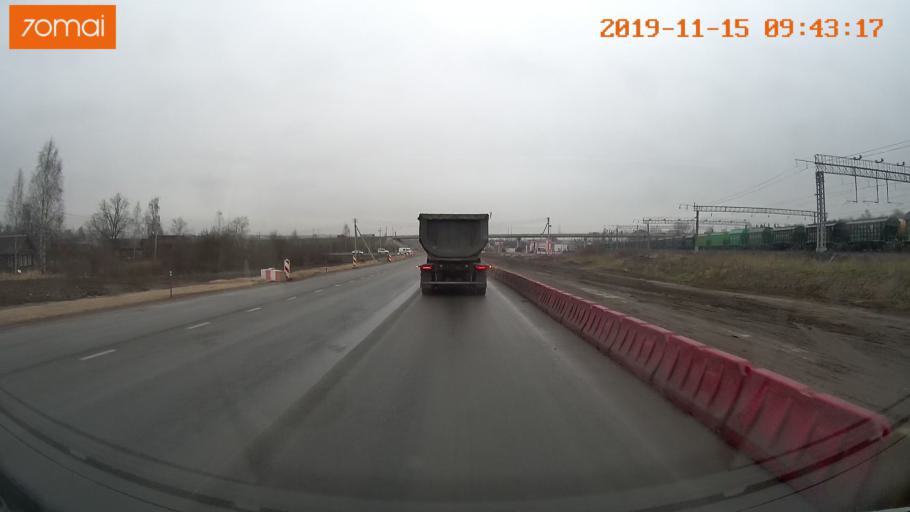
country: RU
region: Vologda
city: Sheksna
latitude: 59.2102
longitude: 38.5092
